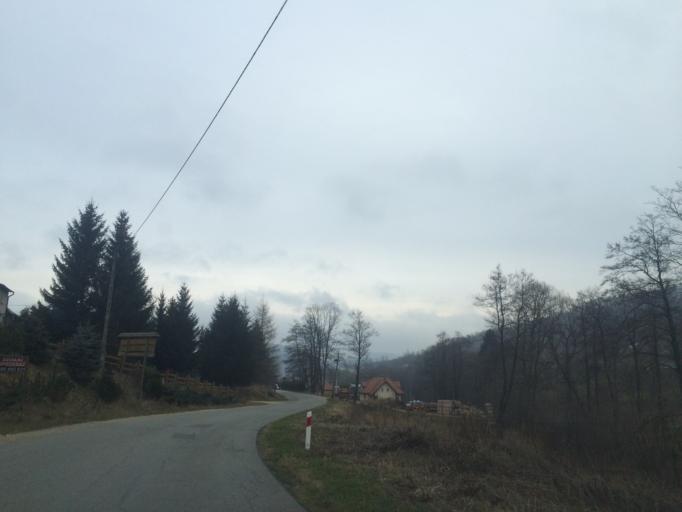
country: PL
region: Lower Silesian Voivodeship
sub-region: Powiat klodzki
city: Stronie Slaskie
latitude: 50.2811
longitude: 16.8503
